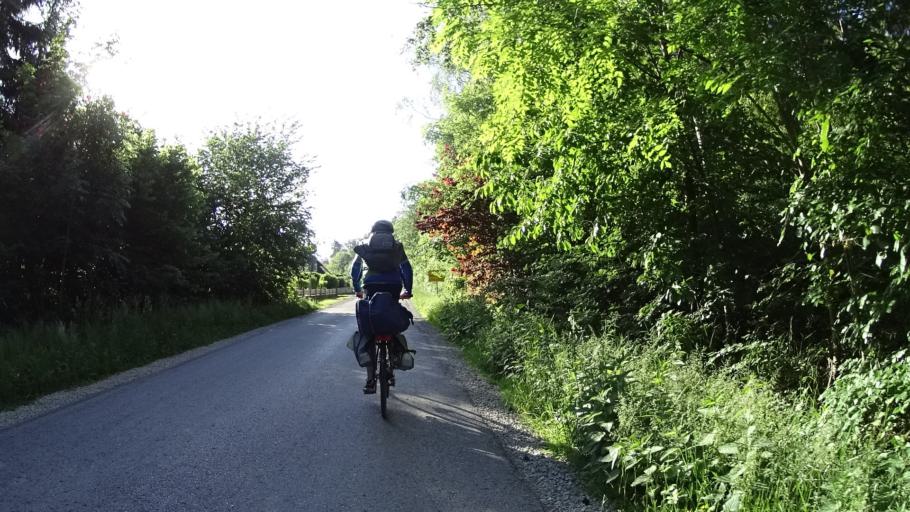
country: DE
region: Bavaria
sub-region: Regierungsbezirk Mittelfranken
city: Dentlein am Forst
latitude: 49.1504
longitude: 10.4081
